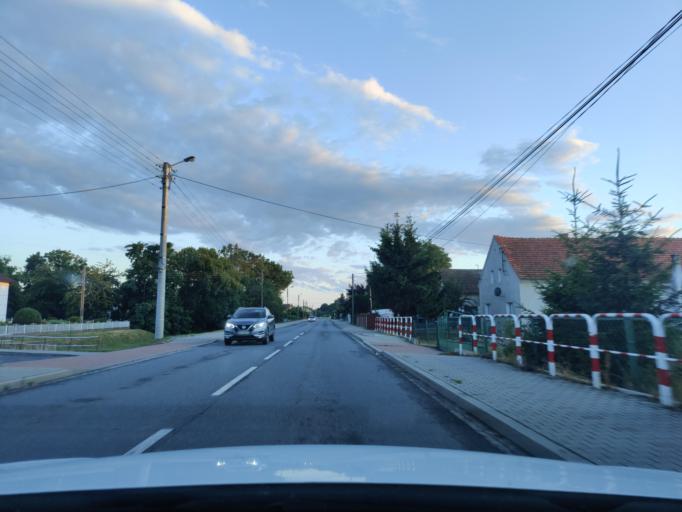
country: PL
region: Opole Voivodeship
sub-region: Powiat nyski
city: Chroscina
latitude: 50.6518
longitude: 17.3857
